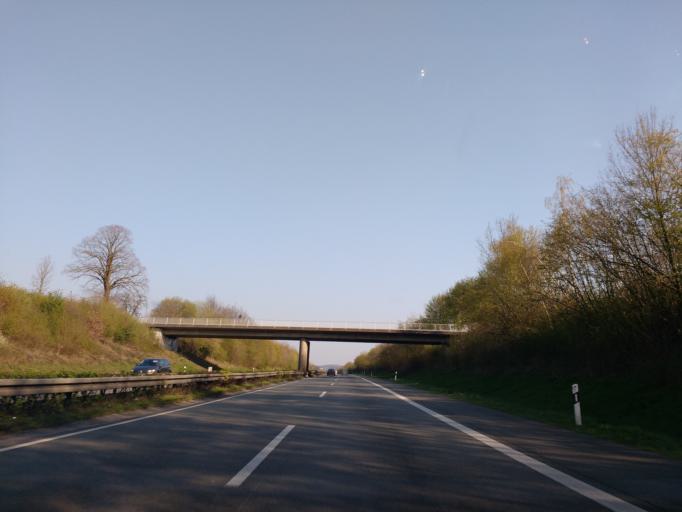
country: DE
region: Lower Saxony
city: Bissendorf
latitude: 52.2180
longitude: 8.1093
